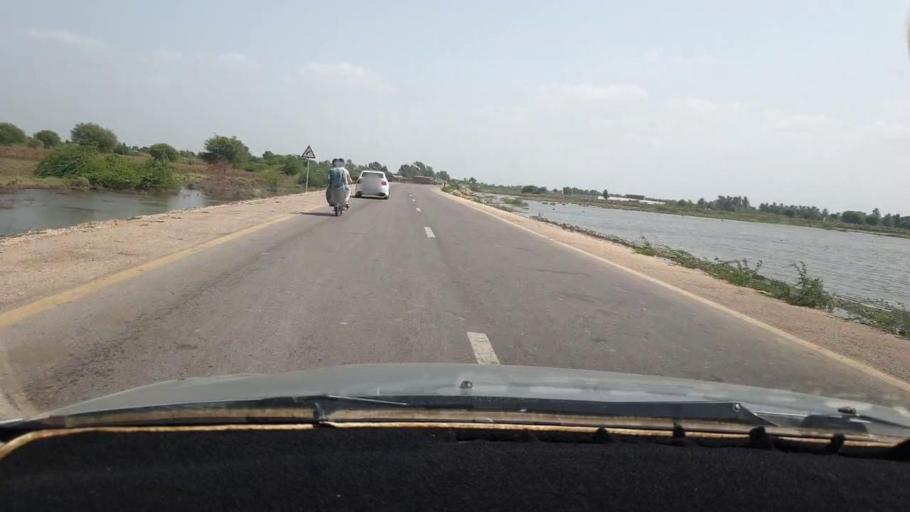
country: PK
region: Sindh
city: Digri
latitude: 25.1550
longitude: 69.1232
